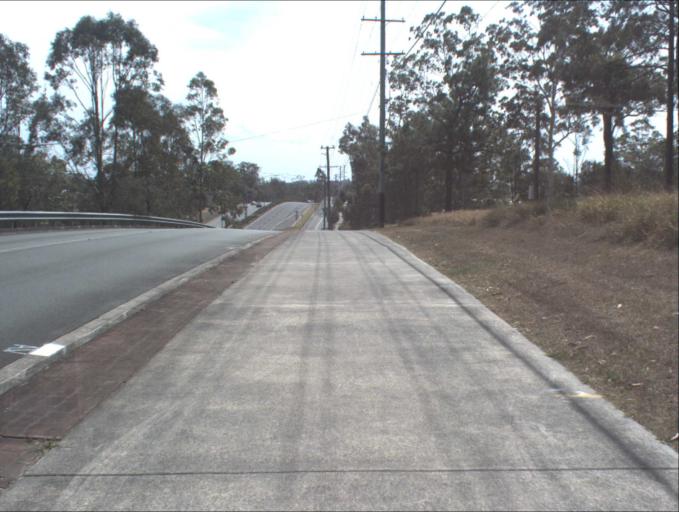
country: AU
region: Queensland
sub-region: Logan
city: Beenleigh
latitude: -27.6701
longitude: 153.2002
